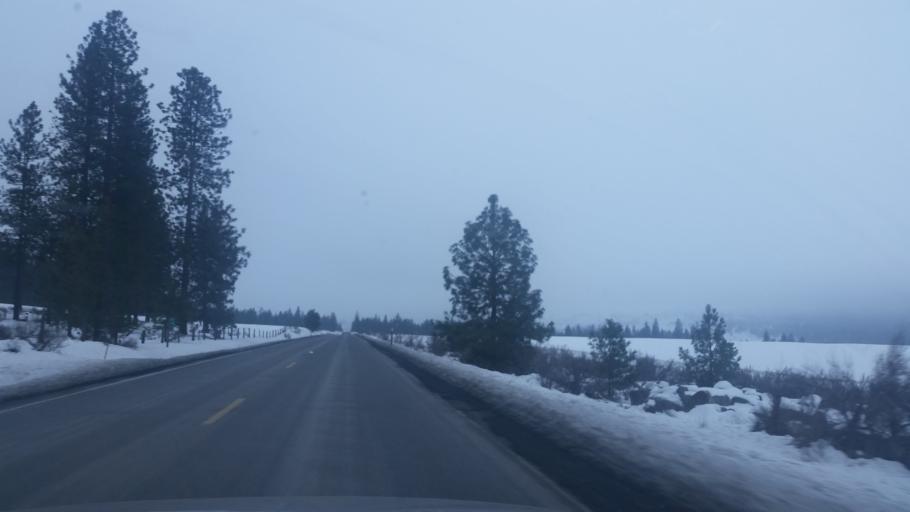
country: US
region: Washington
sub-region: Lincoln County
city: Davenport
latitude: 47.8042
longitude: -117.8926
